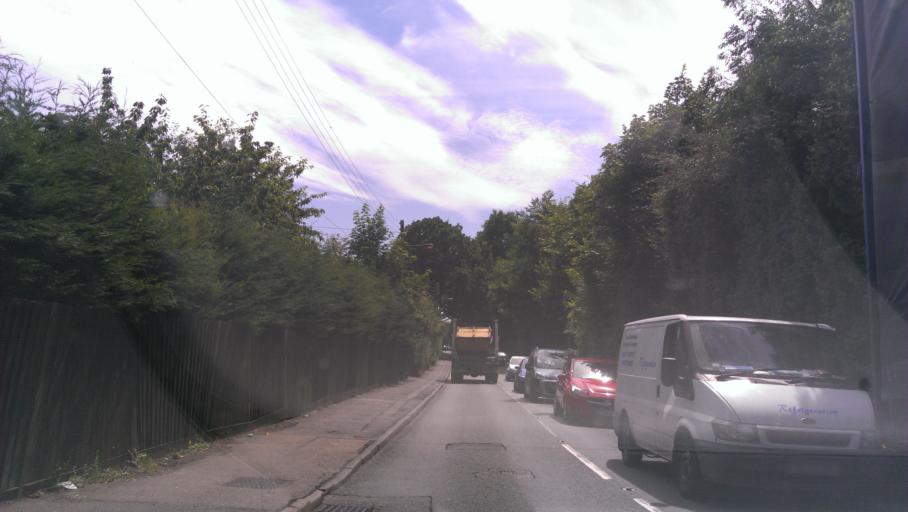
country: GB
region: England
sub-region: Kent
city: Faversham
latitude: 51.3084
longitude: 0.8890
